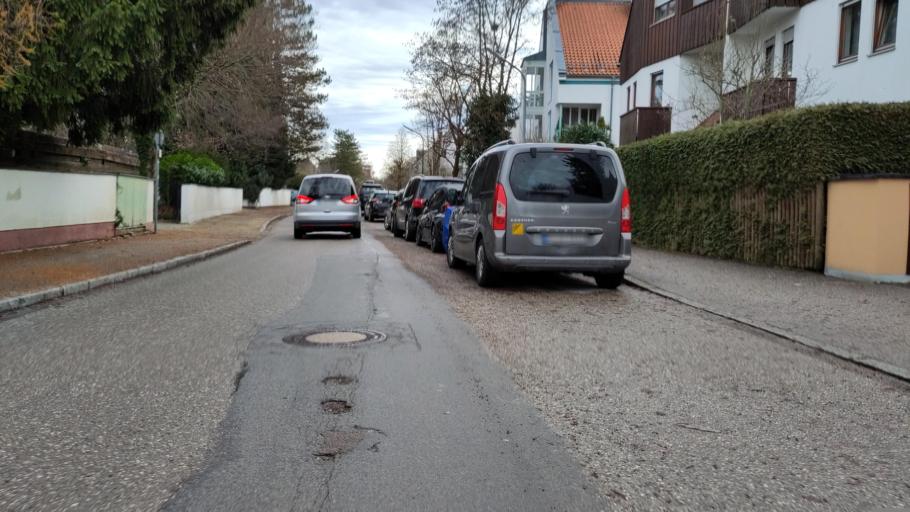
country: DE
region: Bavaria
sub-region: Upper Bavaria
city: Neuried
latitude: 48.0849
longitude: 11.4788
